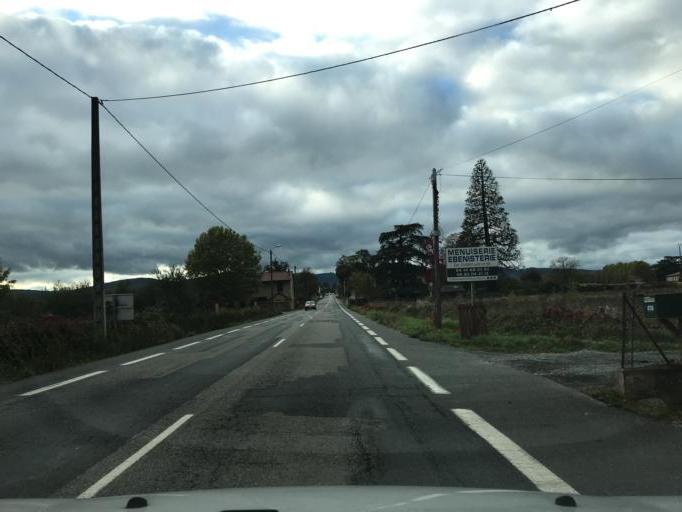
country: FR
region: Rhone-Alpes
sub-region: Departement du Rhone
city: Gleize
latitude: 45.9936
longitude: 4.6834
